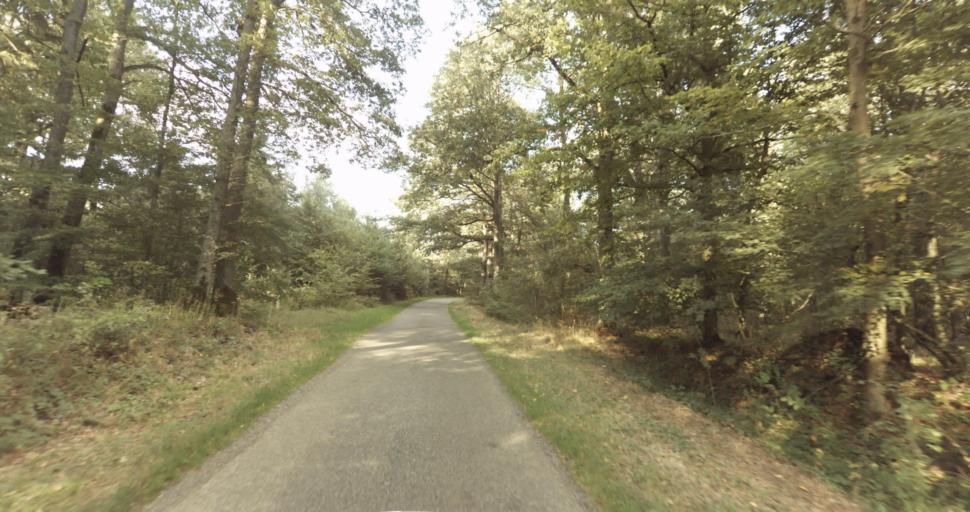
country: FR
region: Haute-Normandie
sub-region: Departement de l'Eure
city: Marcilly-sur-Eure
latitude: 48.8693
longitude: 1.2999
